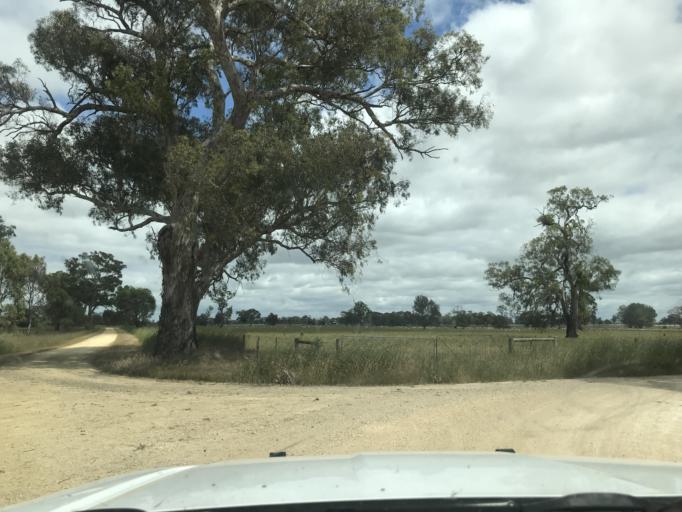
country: AU
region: South Australia
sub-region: Naracoorte and Lucindale
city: Naracoorte
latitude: -37.0055
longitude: 141.1091
